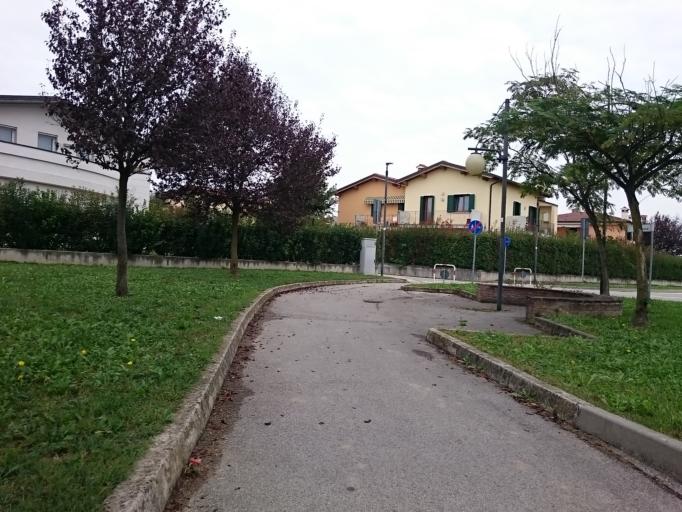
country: IT
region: Veneto
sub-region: Provincia di Vicenza
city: Quinto Vicentino
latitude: 45.5739
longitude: 11.6329
